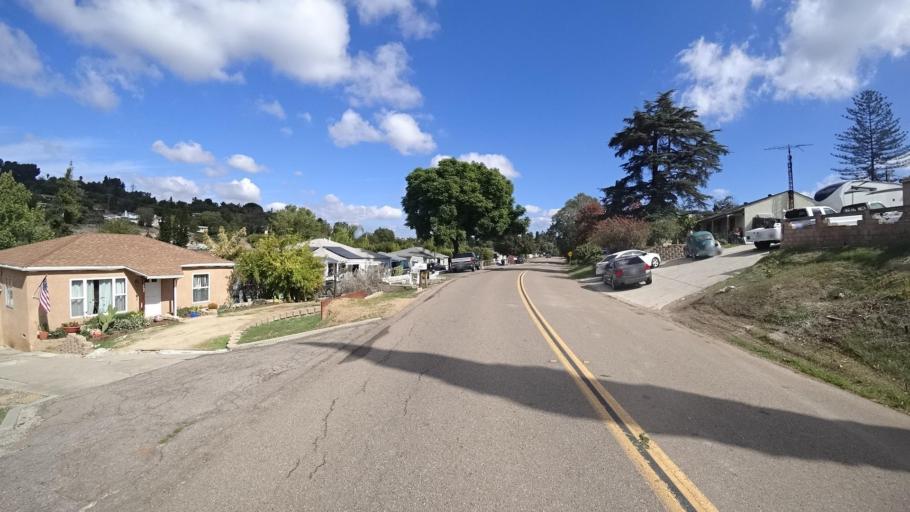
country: US
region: California
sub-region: San Diego County
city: Casa de Oro-Mount Helix
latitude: 32.7430
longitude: -116.9699
